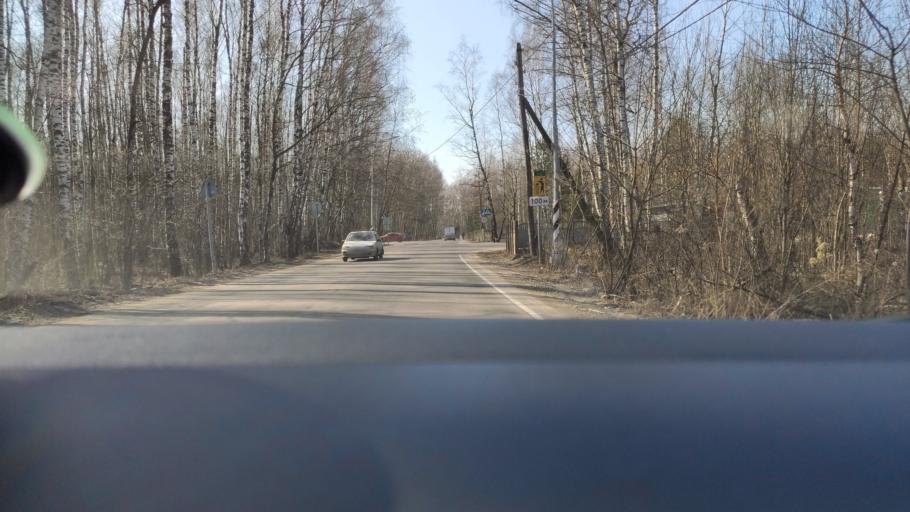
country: RU
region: Moskovskaya
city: Elektrostal'
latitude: 55.7711
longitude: 38.4097
